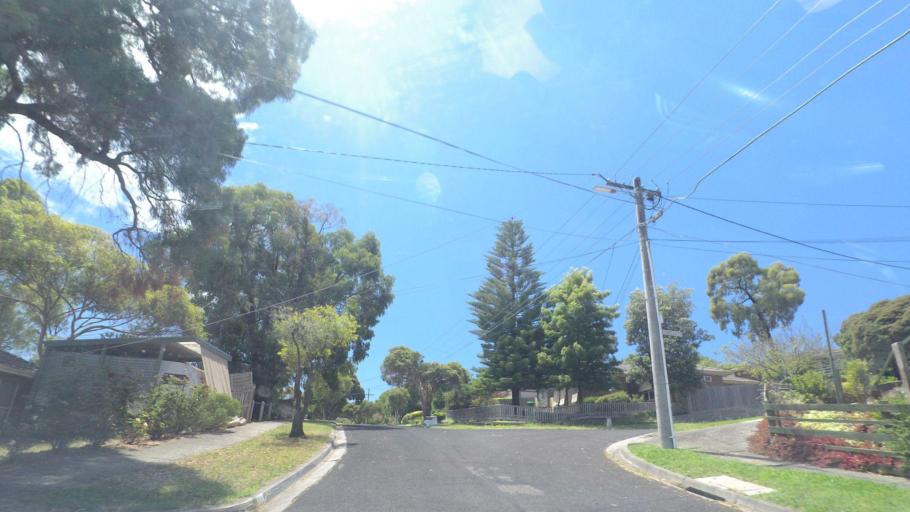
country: AU
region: Victoria
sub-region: Maroondah
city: Croydon North
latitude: -37.7731
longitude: 145.3185
